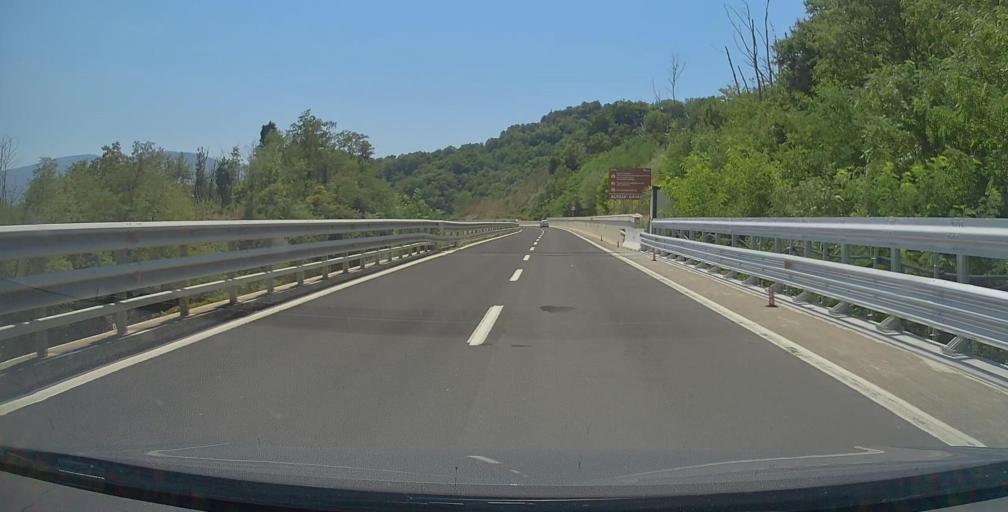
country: IT
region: Calabria
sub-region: Provincia di Cosenza
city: Altilia
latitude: 39.1247
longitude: 16.2591
